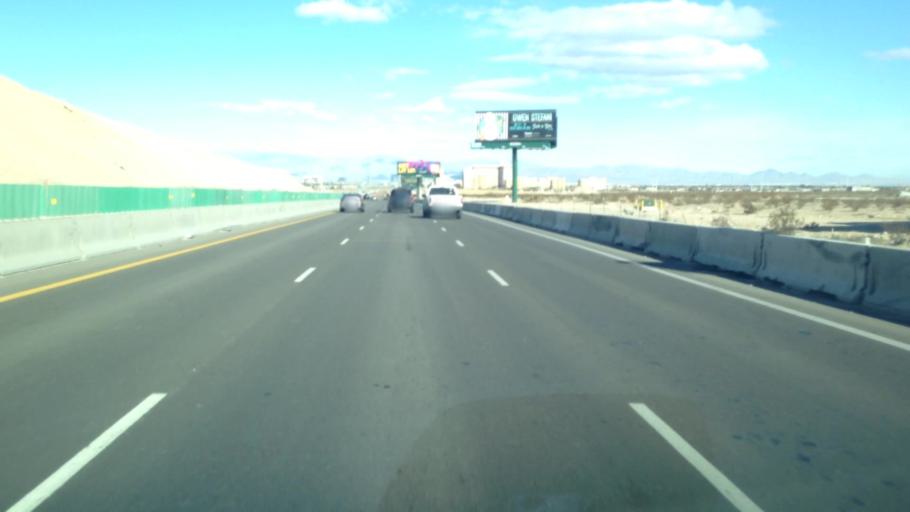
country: US
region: Nevada
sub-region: Clark County
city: Enterprise
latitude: 35.9846
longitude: -115.1803
